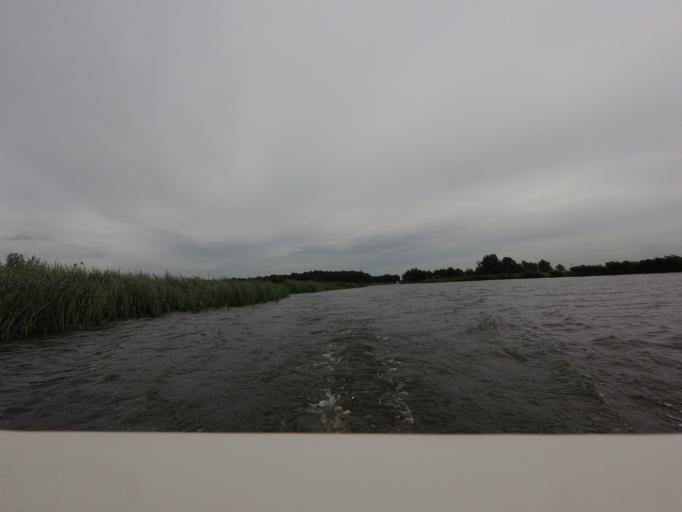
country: NL
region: Friesland
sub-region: Gemeente Boarnsterhim
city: Grou
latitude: 53.1117
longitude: 5.8768
